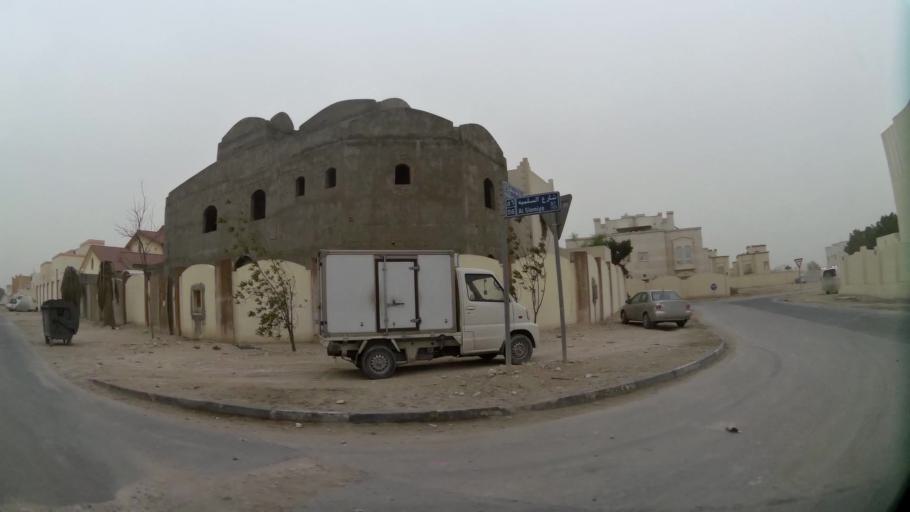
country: QA
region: Baladiyat ad Dawhah
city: Doha
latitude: 25.2346
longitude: 51.5000
